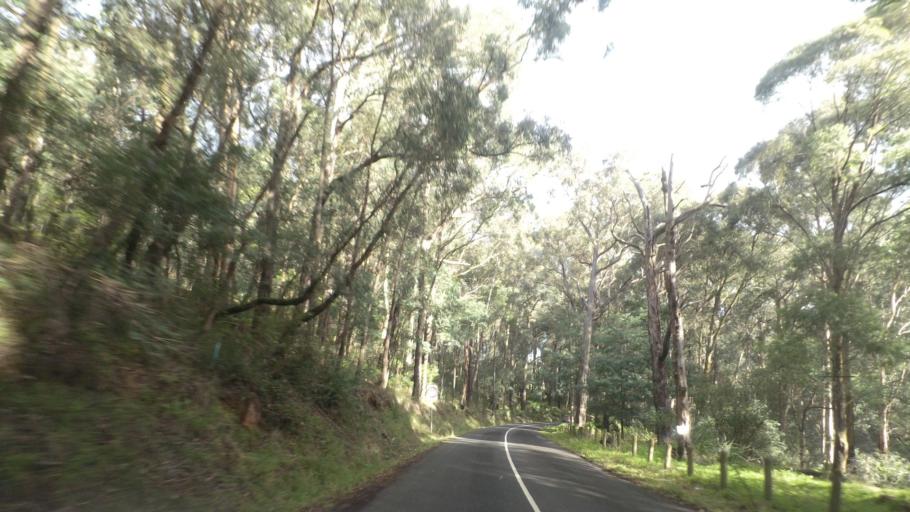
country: AU
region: Victoria
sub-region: Cardinia
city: Emerald
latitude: -37.9090
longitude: 145.4426
